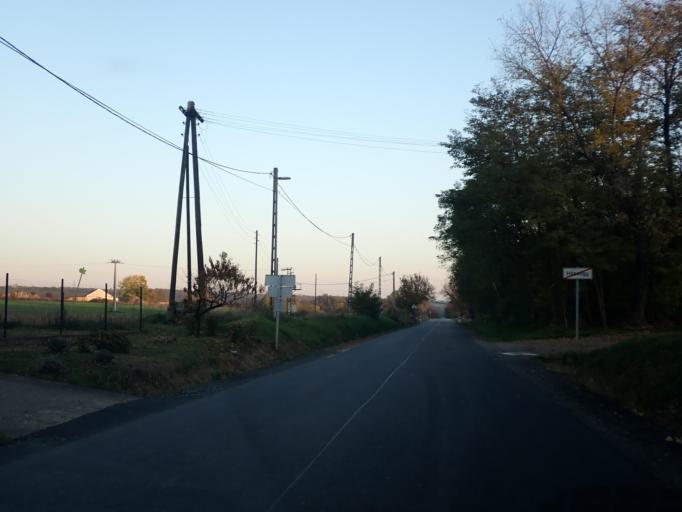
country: HU
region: Baranya
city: Kozarmisleny
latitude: 46.0286
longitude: 18.3920
